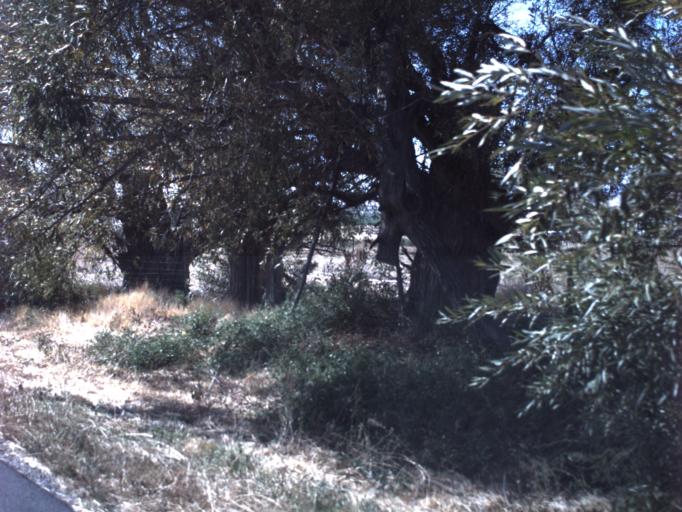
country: US
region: Utah
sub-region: Tooele County
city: Grantsville
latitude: 40.4944
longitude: -112.7481
